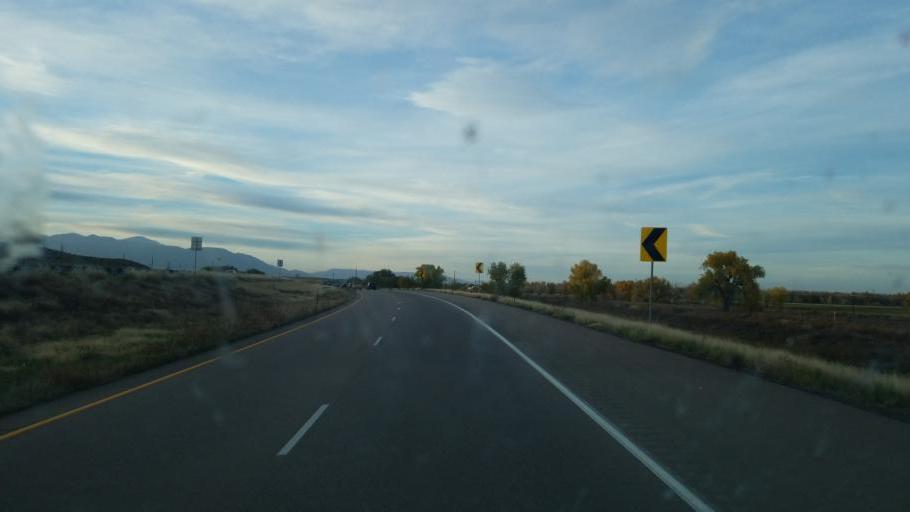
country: US
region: Colorado
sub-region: El Paso County
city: Fountain
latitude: 38.5712
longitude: -104.6565
